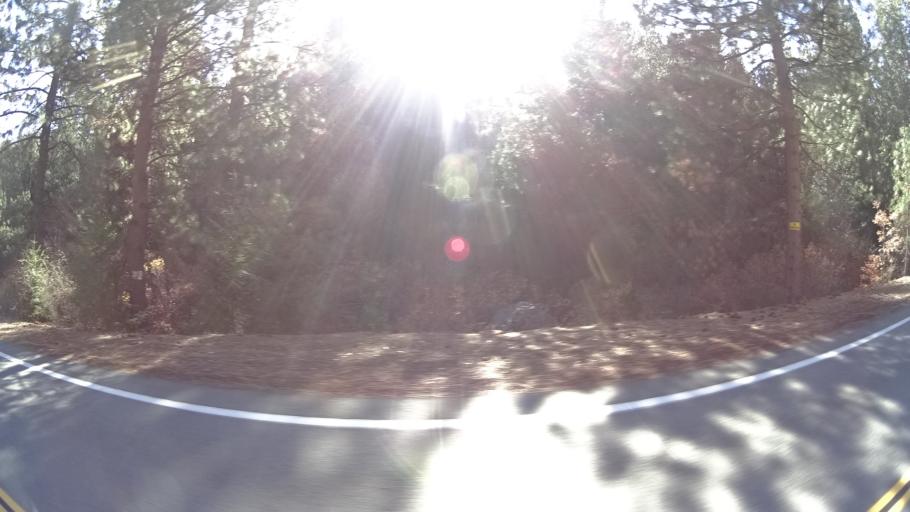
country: US
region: California
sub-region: Siskiyou County
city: Weed
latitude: 41.4577
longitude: -122.6306
